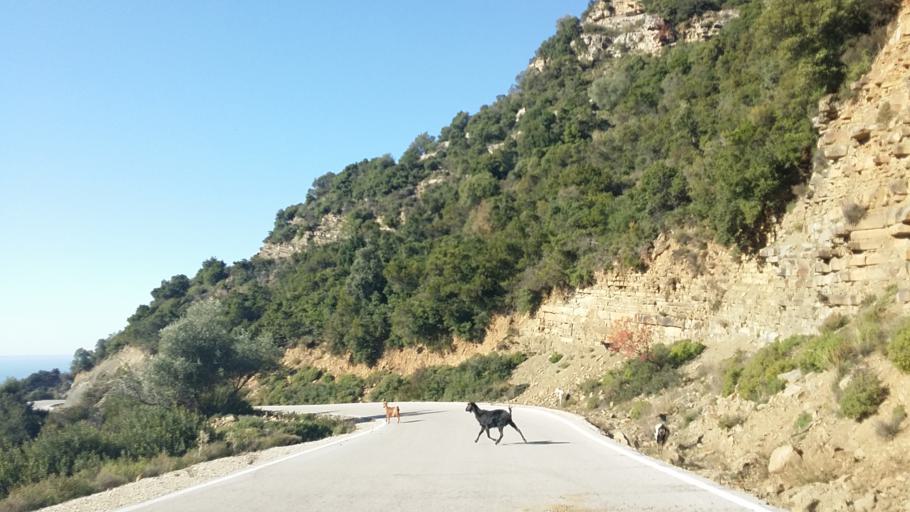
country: GR
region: West Greece
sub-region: Nomos Aitolias kai Akarnanias
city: Krikellos
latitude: 38.9547
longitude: 21.2427
